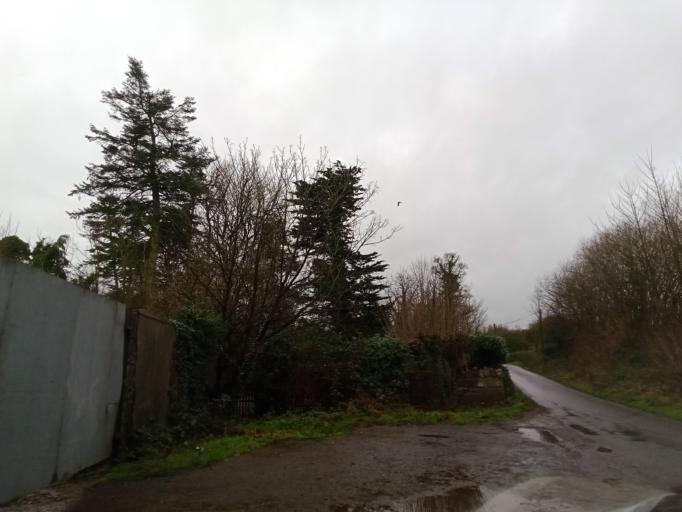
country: IE
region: Munster
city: Fethard
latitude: 52.5651
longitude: -7.7181
